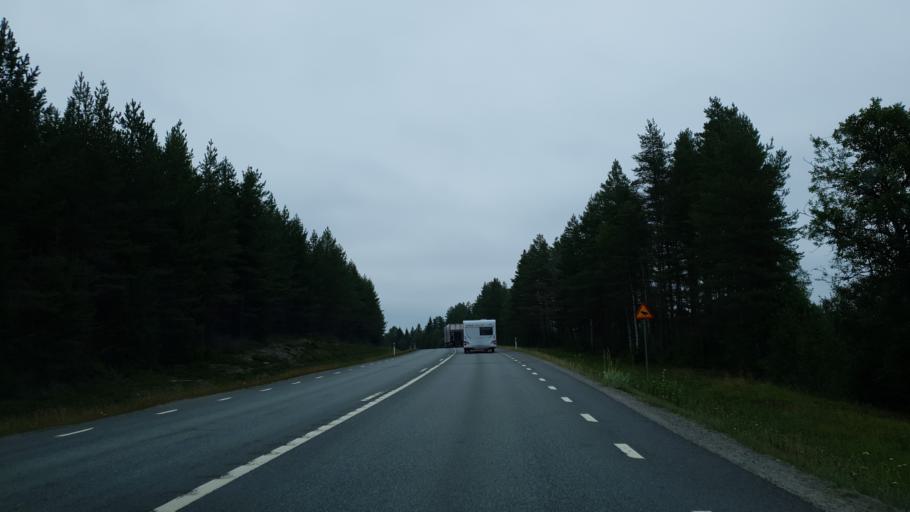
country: SE
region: Vaesterbotten
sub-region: Skelleftea Kommun
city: Burea
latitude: 64.3472
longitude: 21.2893
